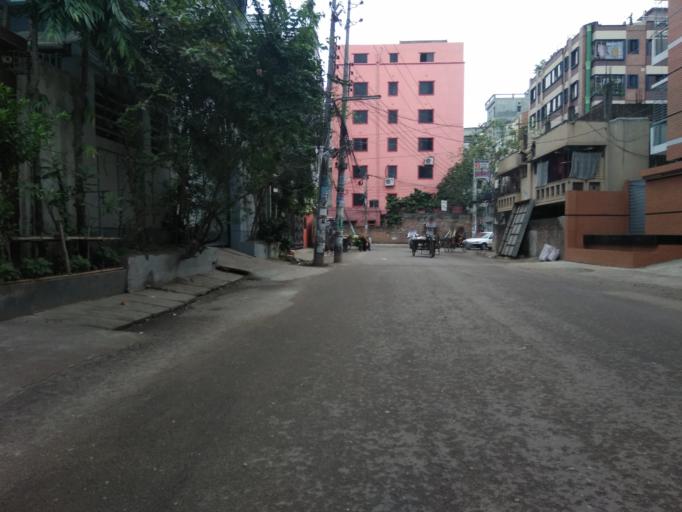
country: BD
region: Dhaka
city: Tungi
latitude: 23.8234
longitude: 90.3672
